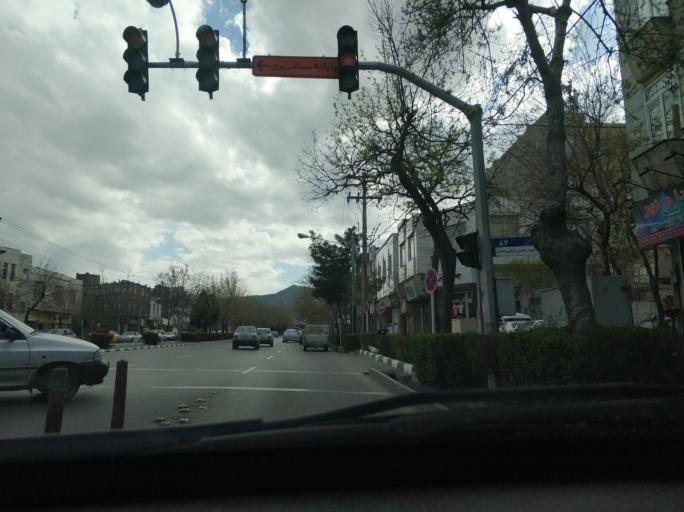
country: IR
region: Razavi Khorasan
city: Mashhad
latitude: 36.2673
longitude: 59.5871
